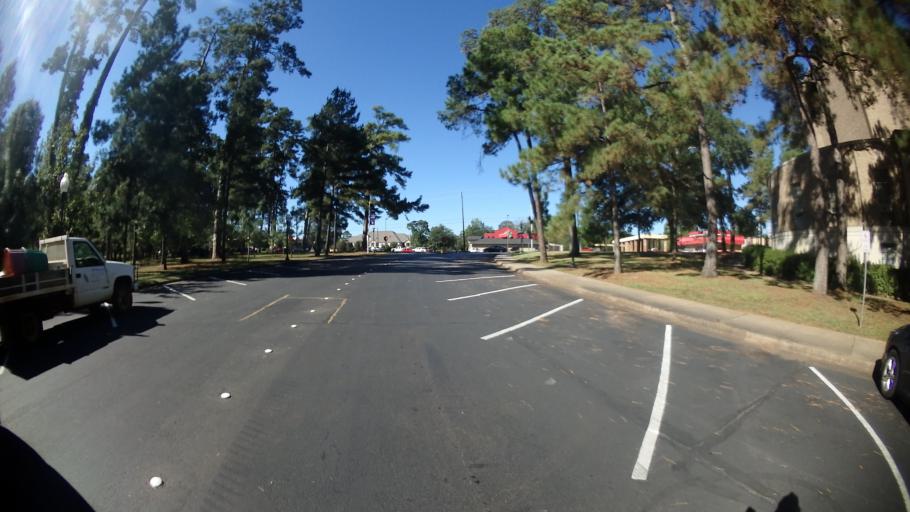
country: US
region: Texas
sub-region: Nacogdoches County
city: Nacogdoches
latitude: 31.6213
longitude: -94.6518
